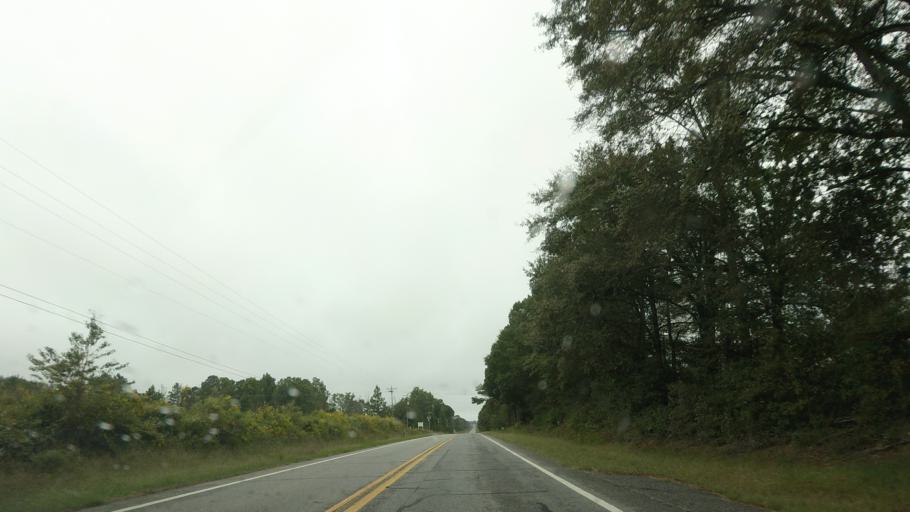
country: US
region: Georgia
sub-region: Irwin County
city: Ocilla
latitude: 31.4852
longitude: -83.2382
